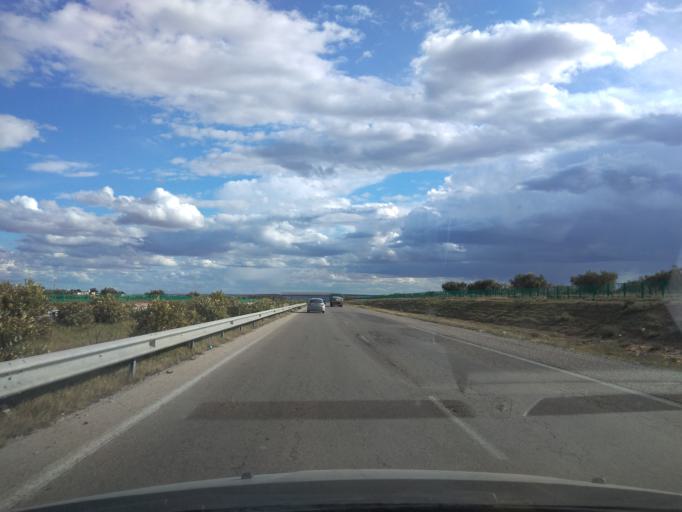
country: TN
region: Al Munastir
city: Manzil Kamil
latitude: 35.5439
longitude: 10.6216
